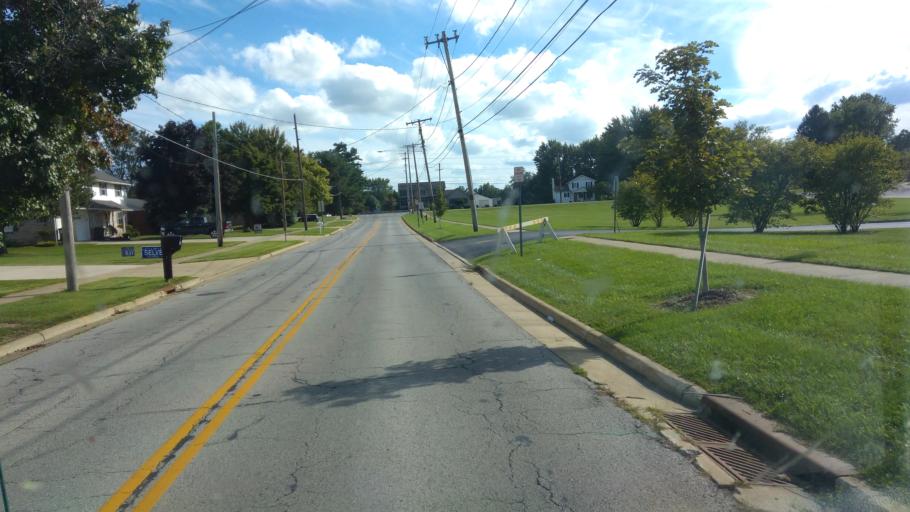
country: US
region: Ohio
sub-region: Sandusky County
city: Clyde
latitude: 41.2899
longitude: -82.9848
